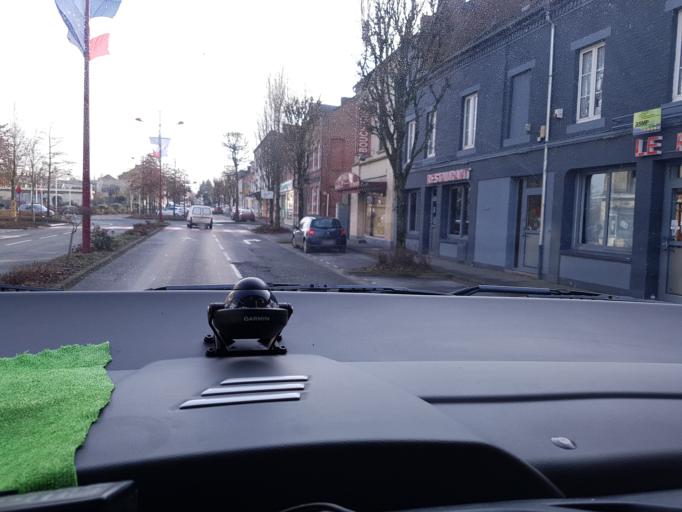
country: FR
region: Picardie
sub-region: Departement de l'Aisne
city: Hirson
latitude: 49.9190
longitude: 4.0847
